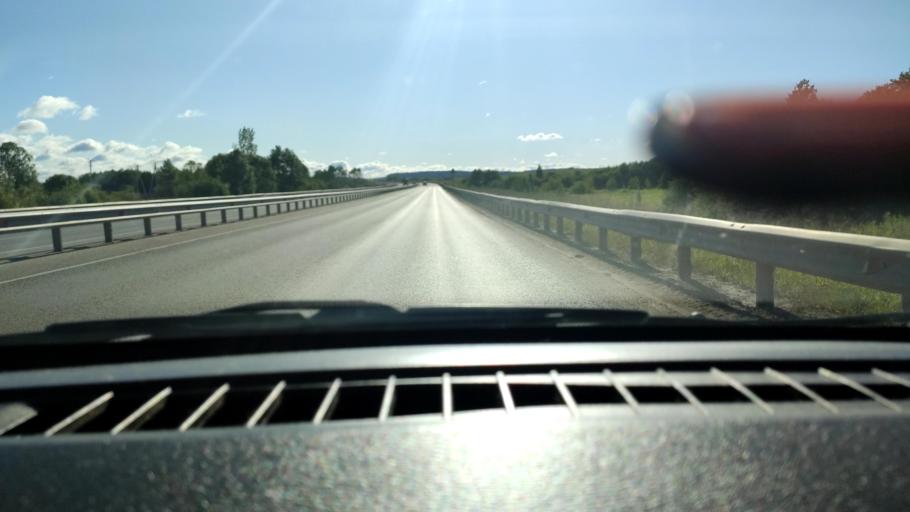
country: RU
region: Perm
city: Kultayevo
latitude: 57.8860
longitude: 55.9319
